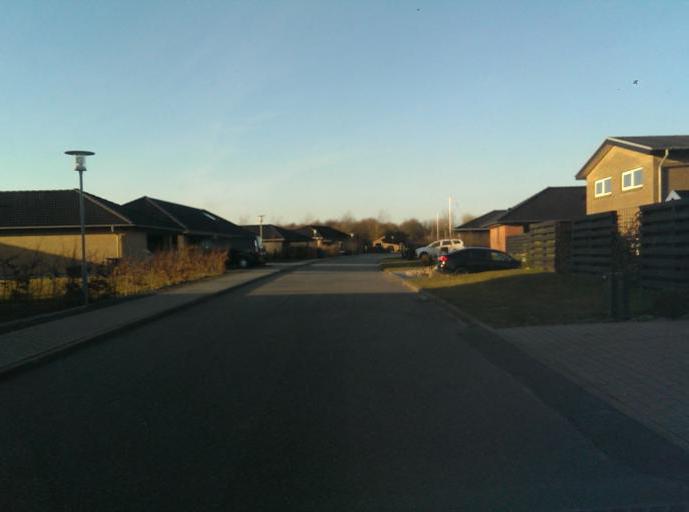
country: DK
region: South Denmark
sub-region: Esbjerg Kommune
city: Esbjerg
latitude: 55.5285
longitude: 8.4087
